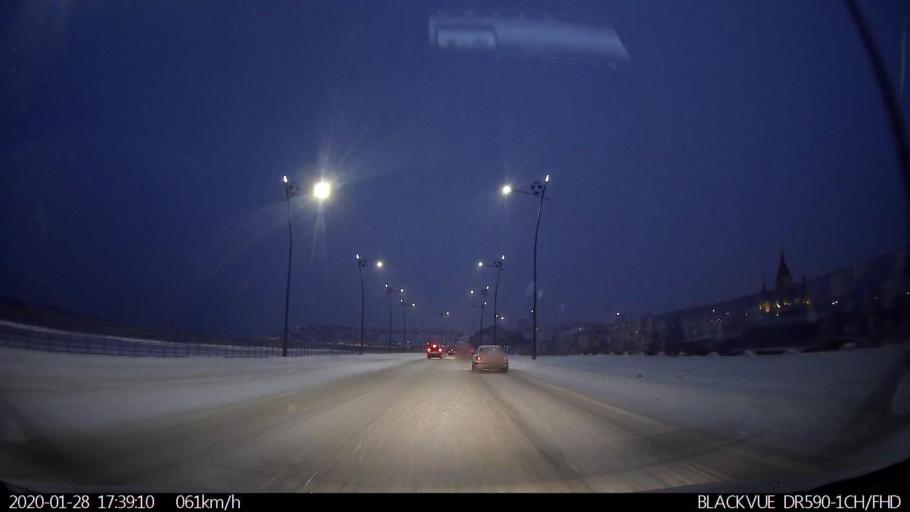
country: RU
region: Nizjnij Novgorod
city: Nizhniy Novgorod
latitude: 56.3372
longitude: 43.9699
